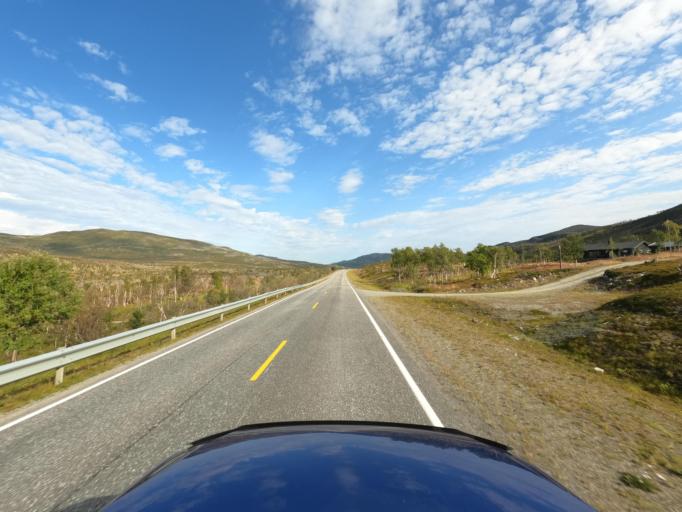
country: NO
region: Finnmark Fylke
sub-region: Kvalsund
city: Kvalsund
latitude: 70.3287
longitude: 24.2613
